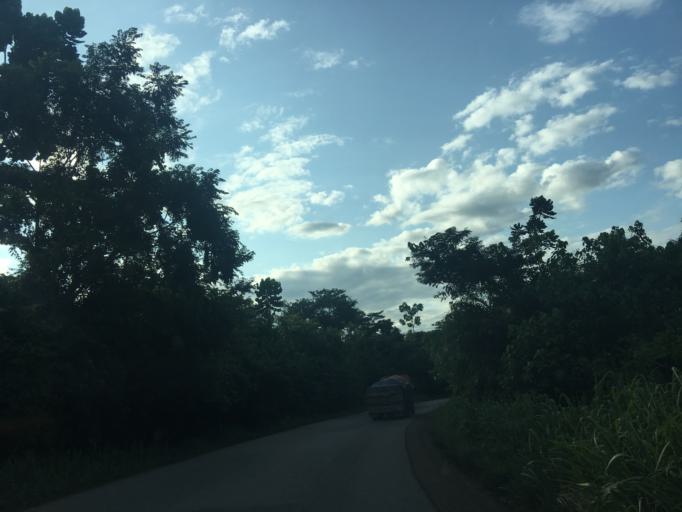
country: GH
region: Western
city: Bibiani
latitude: 6.2848
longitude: -2.2293
